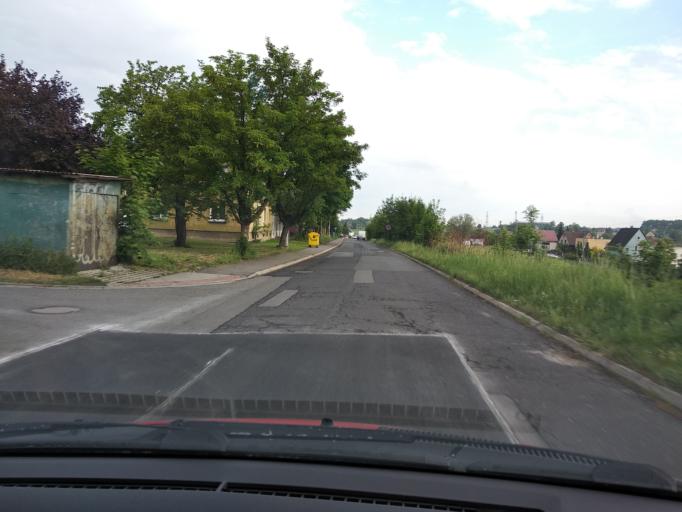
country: CZ
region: Moravskoslezsky
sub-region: Okres Frydek-Mistek
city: Frydek-Mistek
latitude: 49.7001
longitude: 18.3472
